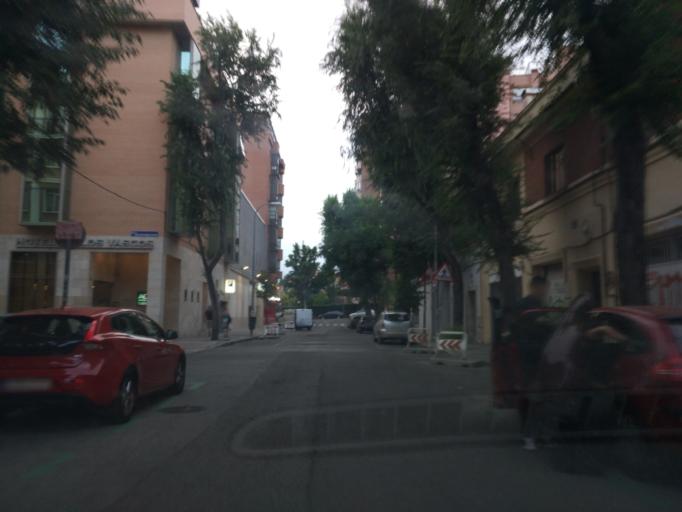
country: ES
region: Madrid
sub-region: Provincia de Madrid
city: Chamberi
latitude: 40.4486
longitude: -3.7112
